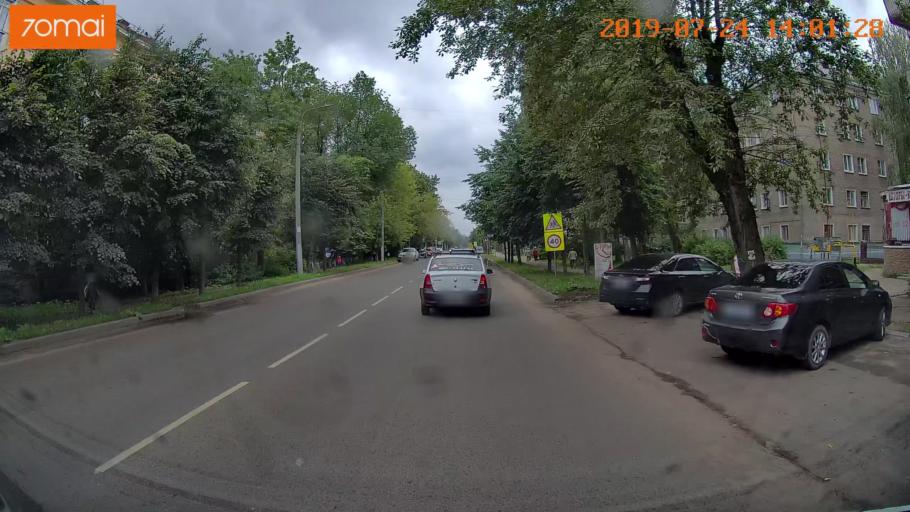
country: RU
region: Ivanovo
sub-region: Gorod Ivanovo
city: Ivanovo
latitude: 57.0099
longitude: 40.9795
